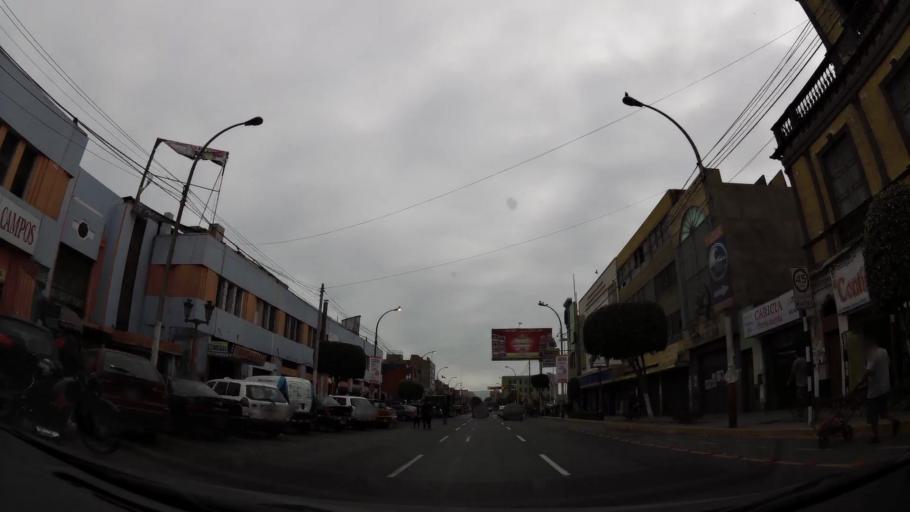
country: PE
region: Callao
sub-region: Callao
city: Callao
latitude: -12.0603
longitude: -77.1390
